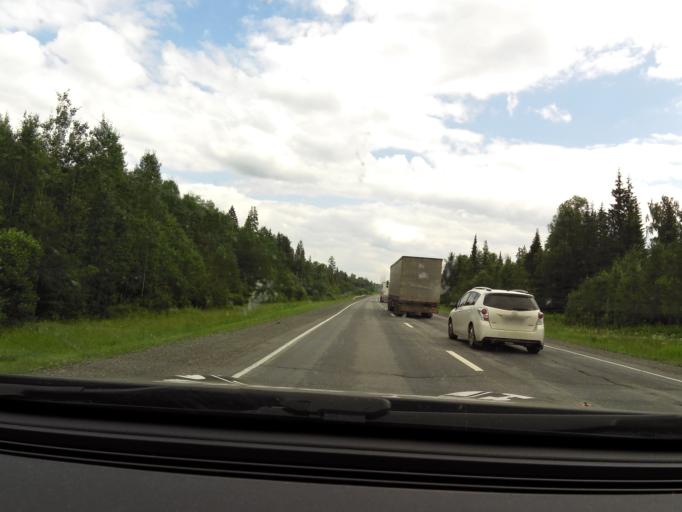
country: RU
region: Sverdlovsk
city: Atig
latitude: 56.8140
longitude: 59.3577
